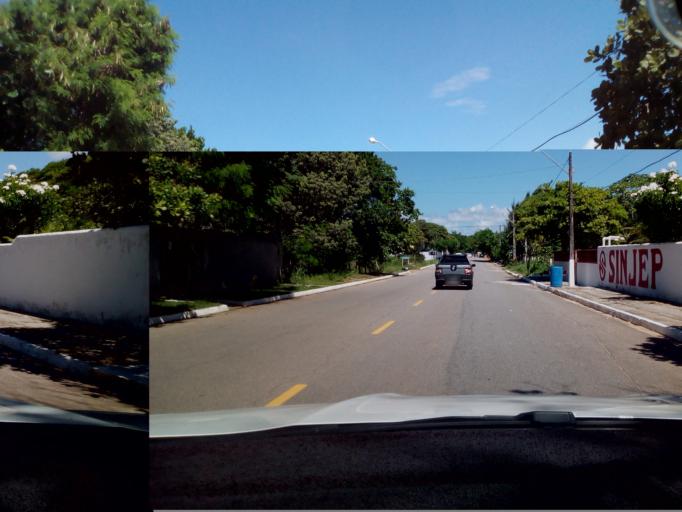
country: BR
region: Paraiba
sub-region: Joao Pessoa
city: Joao Pessoa
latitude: -7.1559
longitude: -34.7956
